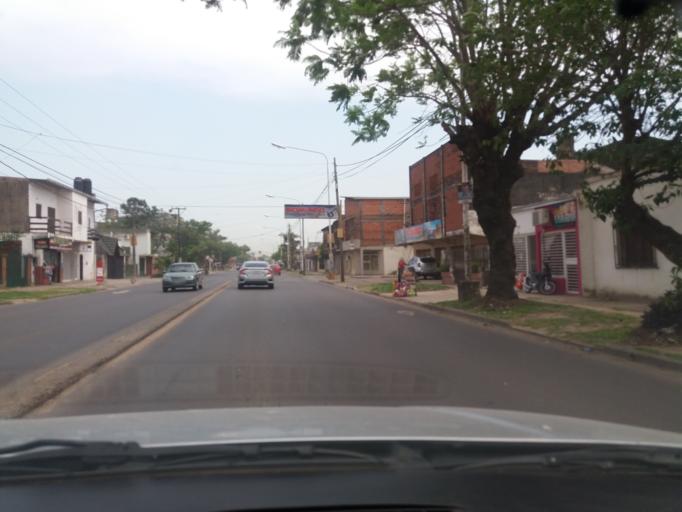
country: AR
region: Corrientes
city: Corrientes
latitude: -27.4935
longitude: -58.8184
